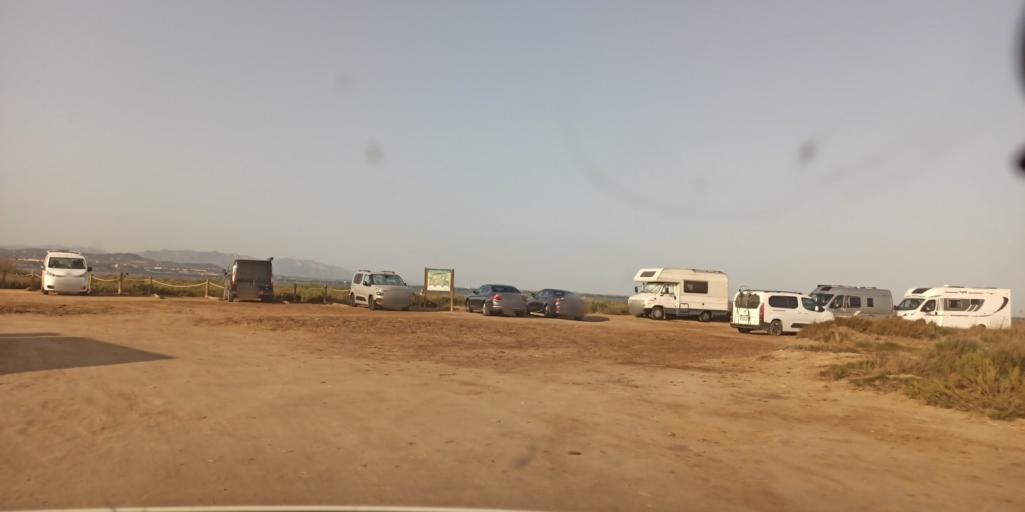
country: ES
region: Catalonia
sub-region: Provincia de Tarragona
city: L'Ampolla
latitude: 40.7787
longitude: 0.7179
